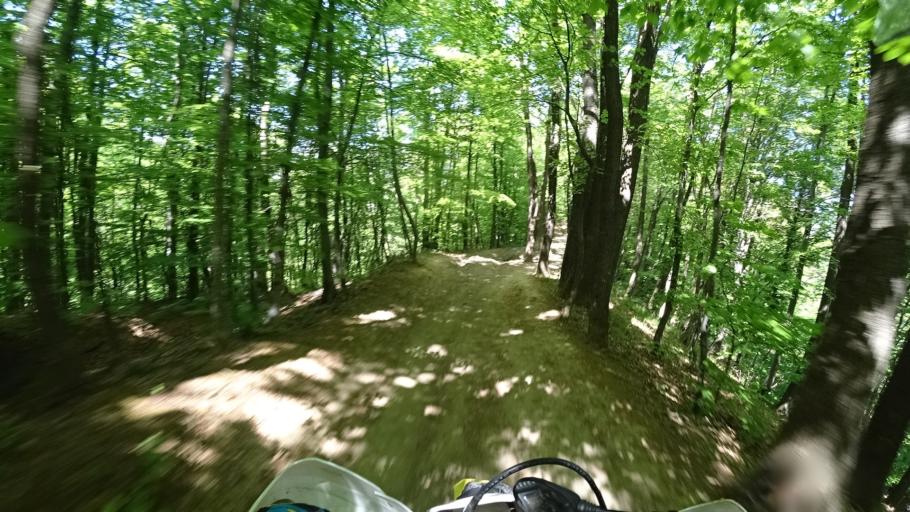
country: HR
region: Zagrebacka
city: Jablanovec
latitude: 45.8669
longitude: 15.8858
